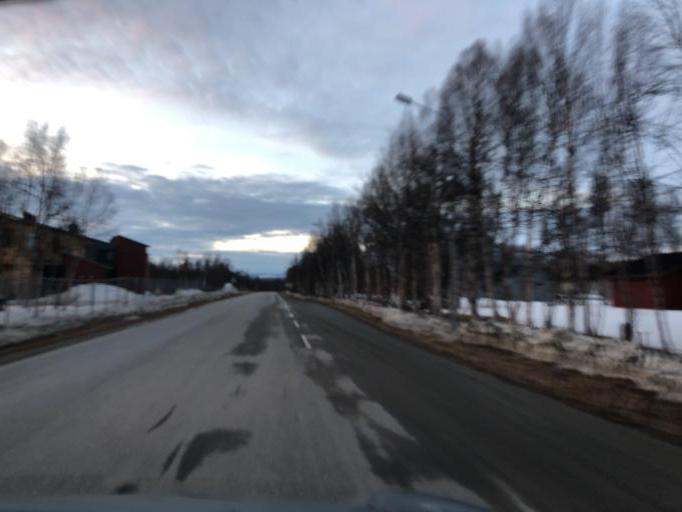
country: NO
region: Sor-Trondelag
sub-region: Tydal
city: Aas
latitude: 62.6482
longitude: 11.8652
